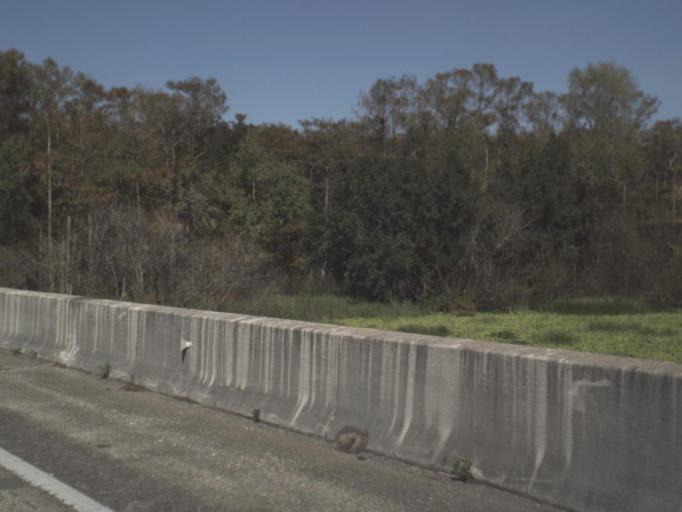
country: US
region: Florida
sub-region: Hendry County
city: Port LaBelle
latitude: 26.9309
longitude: -81.3145
